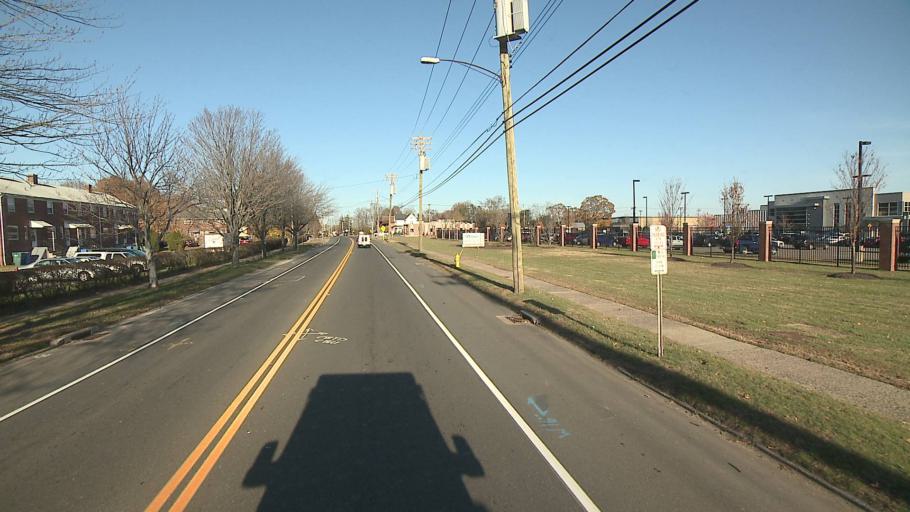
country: US
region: Connecticut
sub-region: New Haven County
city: New Haven
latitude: 41.3367
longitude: -72.8990
